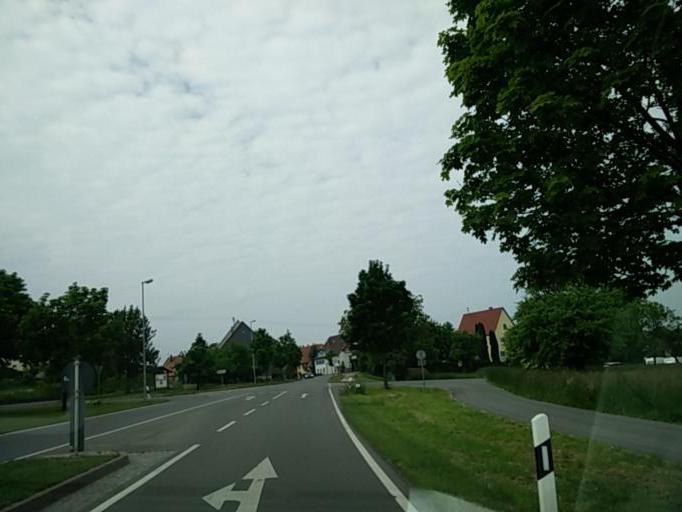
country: DE
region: Baden-Wuerttemberg
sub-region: Tuebingen Region
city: Rottenburg
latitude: 48.4506
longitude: 8.9202
